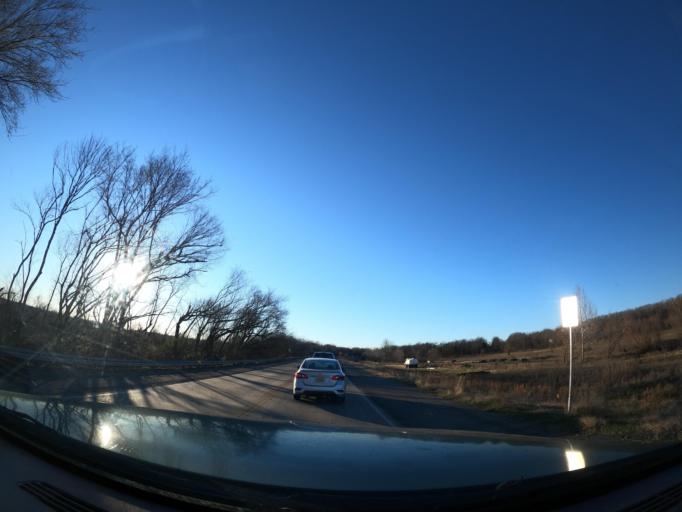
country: US
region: Oklahoma
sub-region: Pittsburg County
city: Hartshorne
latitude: 34.8553
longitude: -95.5866
